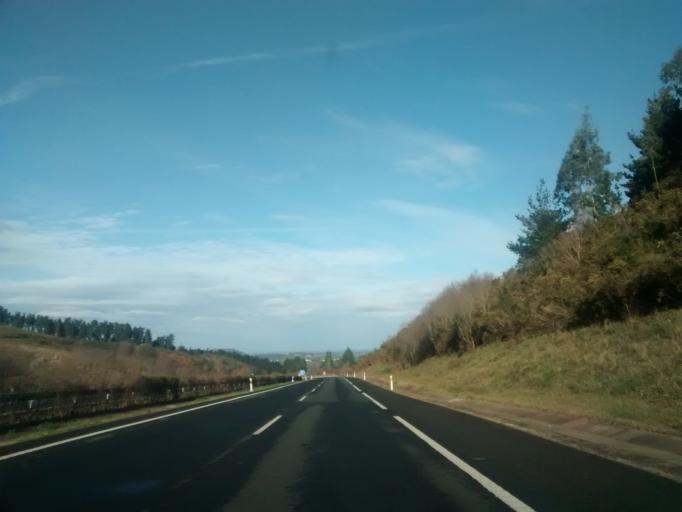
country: ES
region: Cantabria
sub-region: Provincia de Cantabria
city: Comillas
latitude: 43.3303
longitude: -4.3072
